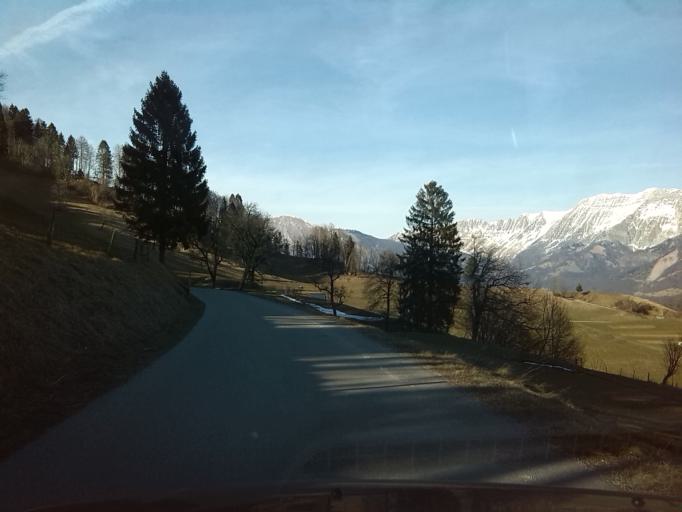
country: IT
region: Friuli Venezia Giulia
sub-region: Provincia di Udine
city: Cras
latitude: 46.2007
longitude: 13.5889
